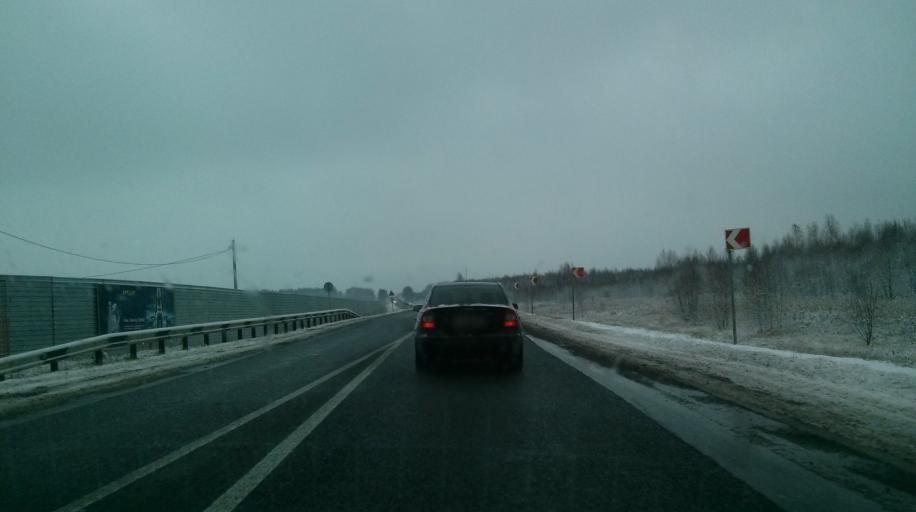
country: RU
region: Nizjnij Novgorod
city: Bogorodsk
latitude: 56.1231
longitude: 43.5969
